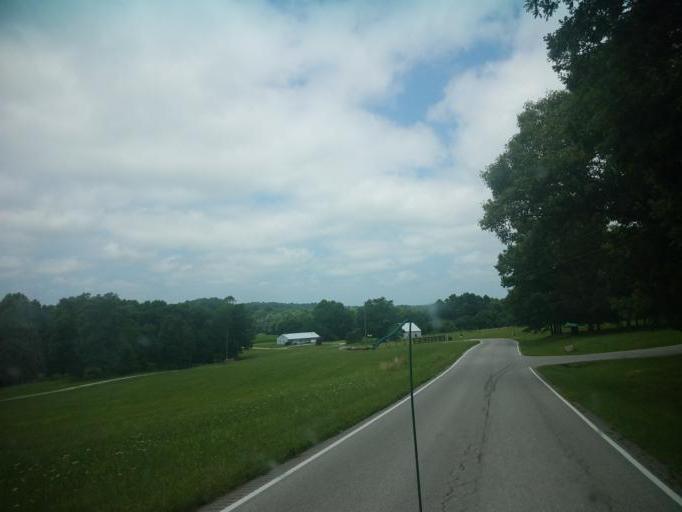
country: US
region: Kentucky
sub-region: Hart County
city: Munfordville
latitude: 37.3371
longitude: -86.0256
